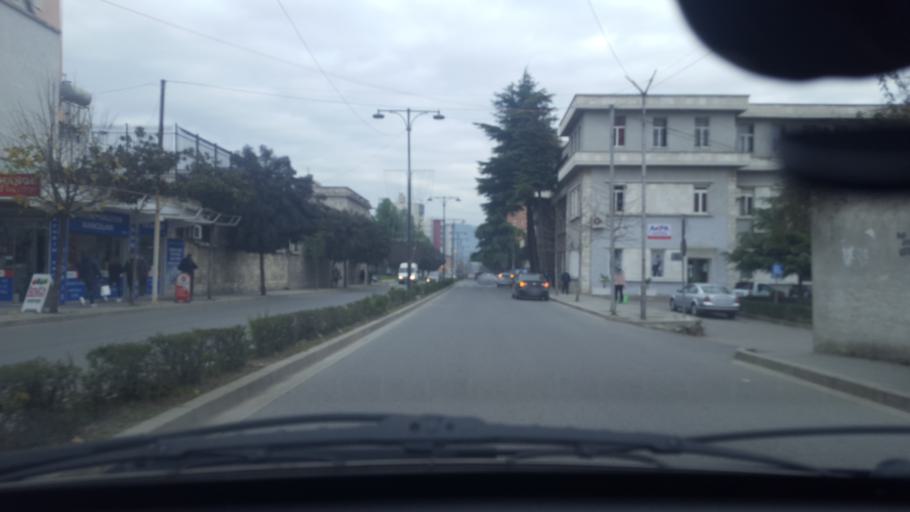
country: AL
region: Elbasan
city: Elbasan
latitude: 41.1107
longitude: 20.0798
